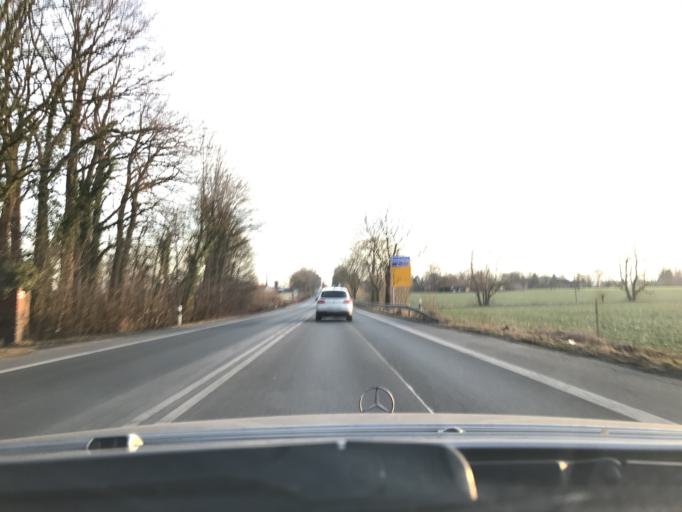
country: DE
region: North Rhine-Westphalia
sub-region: Regierungsbezirk Arnsberg
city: Werl
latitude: 51.6013
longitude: 7.8546
